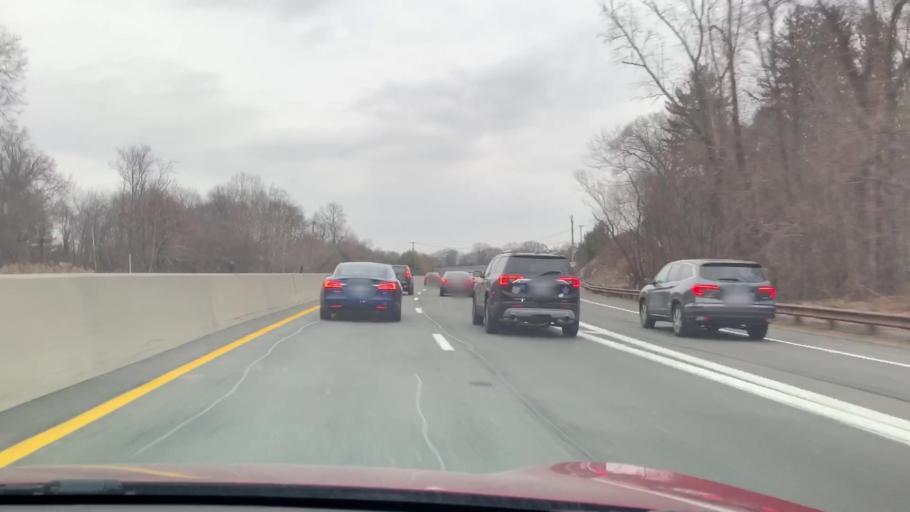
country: US
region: New York
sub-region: Westchester County
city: Rye Brook
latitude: 41.0278
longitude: -73.6872
